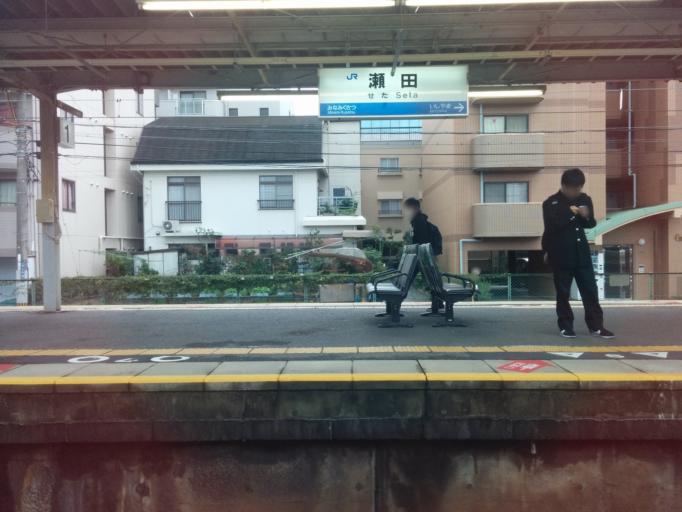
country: JP
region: Shiga Prefecture
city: Kusatsu
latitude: 34.9874
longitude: 135.9262
